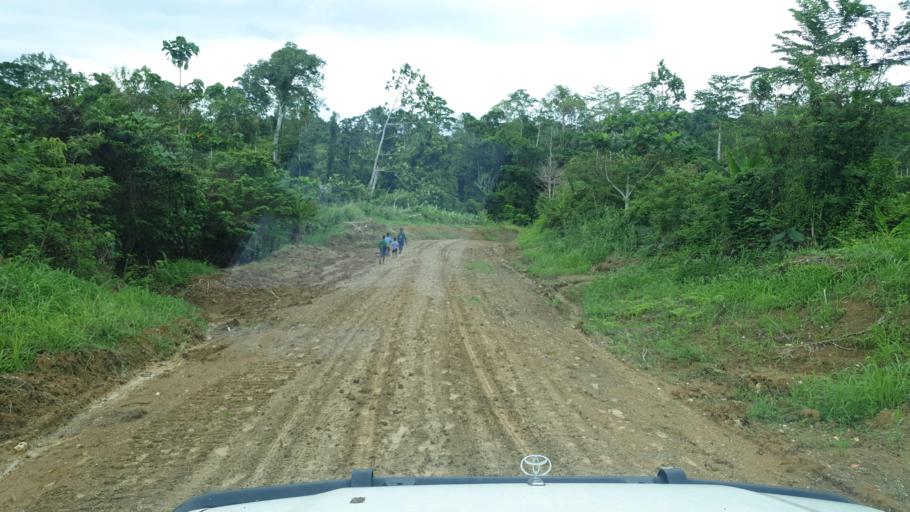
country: PG
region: Gulf
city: Kerema
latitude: -7.9829
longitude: 145.8353
